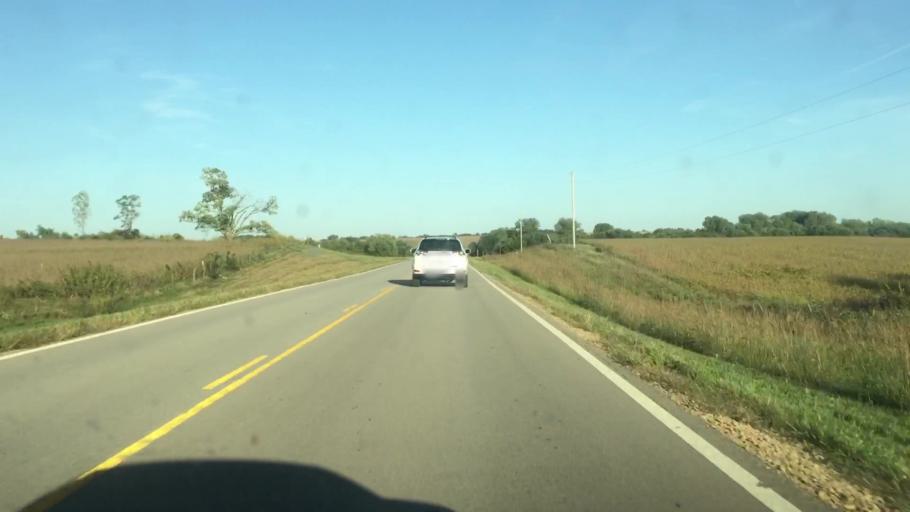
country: US
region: Kansas
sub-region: Brown County
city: Horton
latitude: 39.5874
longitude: -95.5383
